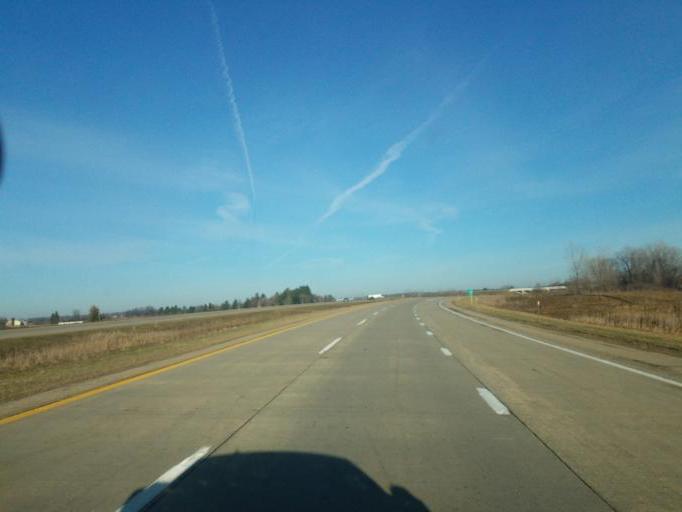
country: US
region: Michigan
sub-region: Clinton County
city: Saint Johns
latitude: 43.0245
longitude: -84.5550
